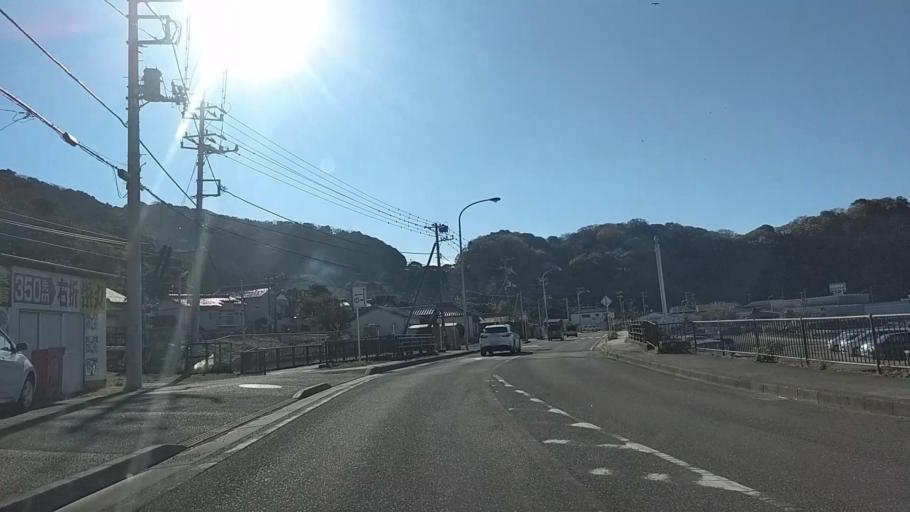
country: JP
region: Chiba
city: Tateyama
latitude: 35.1314
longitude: 139.8398
